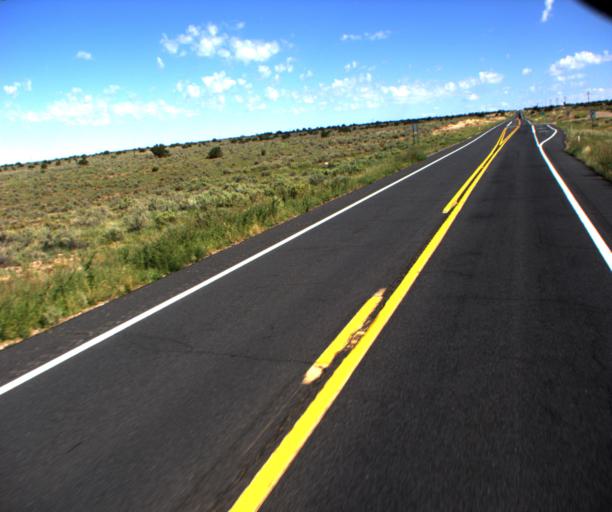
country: US
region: Arizona
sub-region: Coconino County
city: Grand Canyon Village
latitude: 35.7284
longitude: -112.1311
